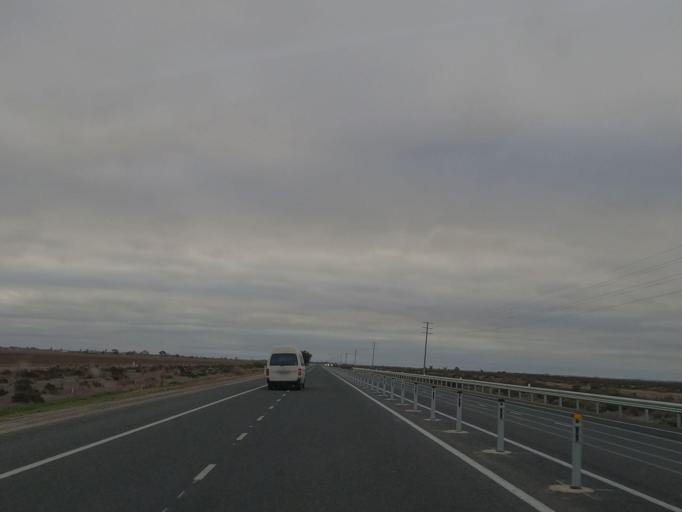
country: AU
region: Victoria
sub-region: Swan Hill
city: Swan Hill
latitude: -35.5073
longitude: 143.7214
